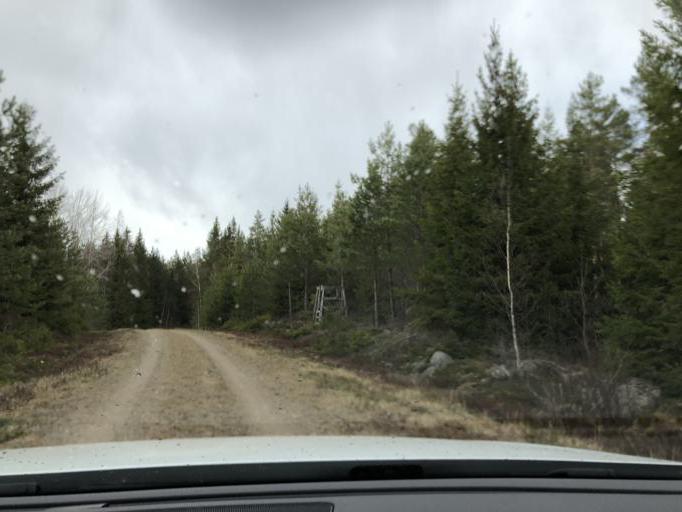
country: SE
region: Gaevleborg
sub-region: Gavle Kommun
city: Hedesunda
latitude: 60.3396
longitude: 17.0648
